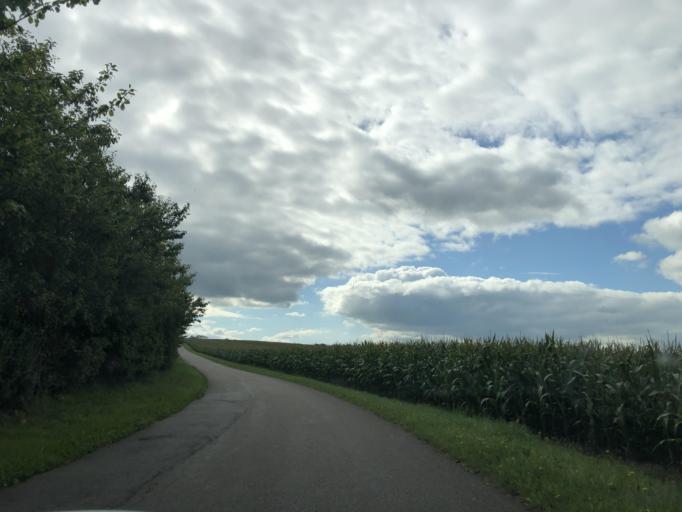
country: DK
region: North Denmark
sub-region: Vesthimmerland Kommune
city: Aars
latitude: 56.8230
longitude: 9.6566
